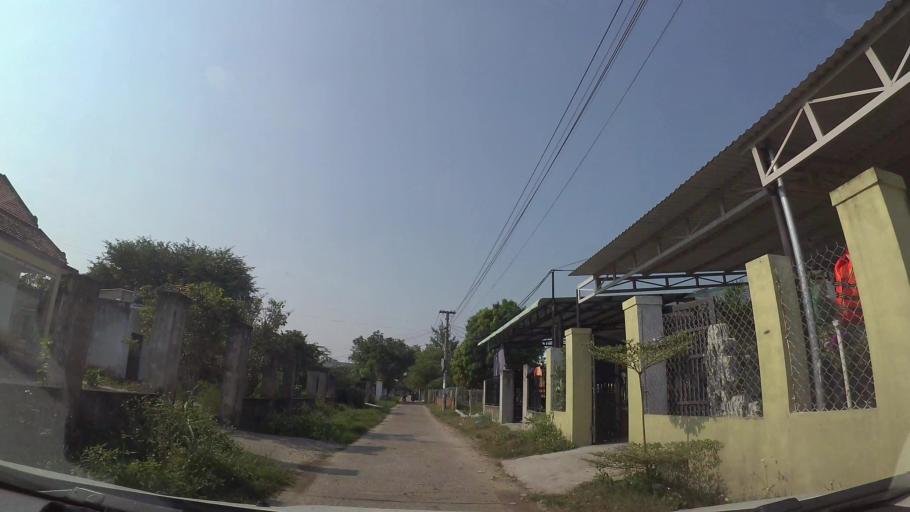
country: VN
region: Da Nang
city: Ngu Hanh Son
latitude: 15.9536
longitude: 108.2659
